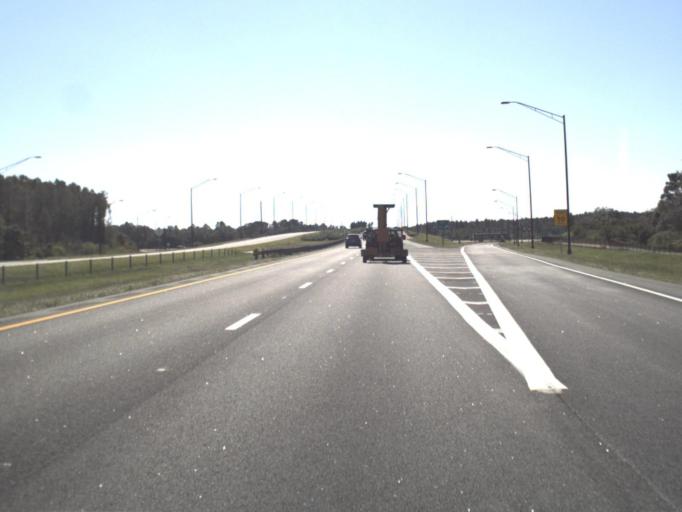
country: US
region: Florida
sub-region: Pasco County
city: Shady Hills
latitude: 28.3358
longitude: -82.5518
